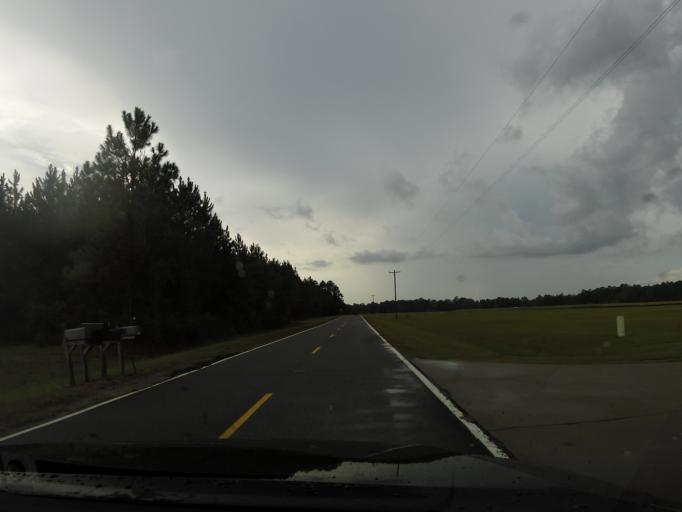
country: US
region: Georgia
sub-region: Wayne County
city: Jesup
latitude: 31.5530
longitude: -81.8872
